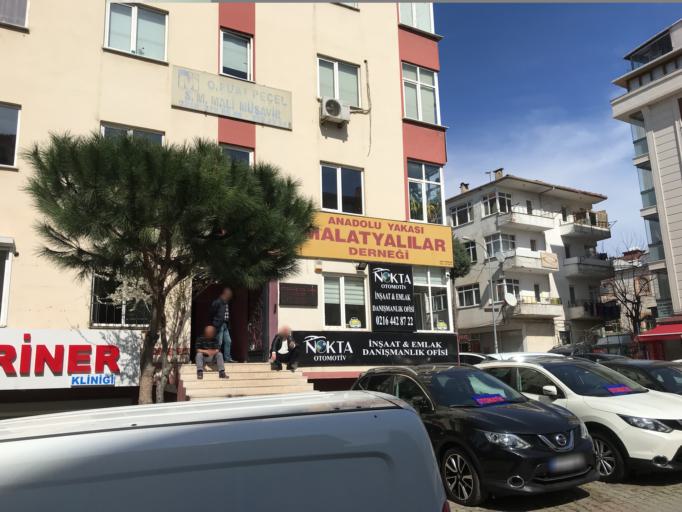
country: TR
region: Istanbul
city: Maltepe
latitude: 40.9279
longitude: 29.1321
